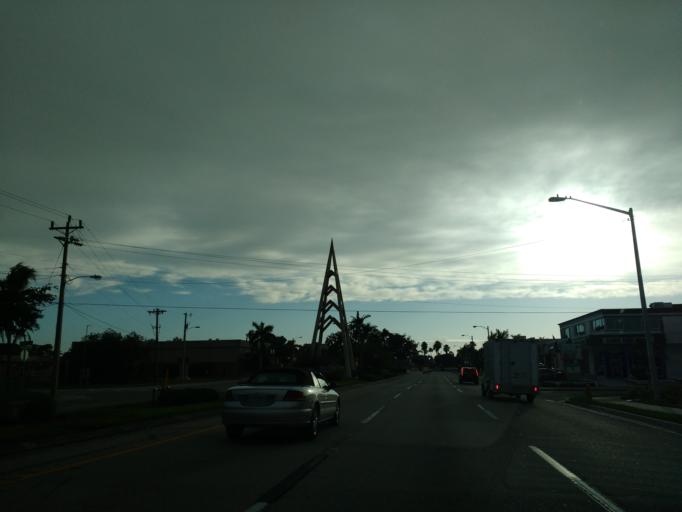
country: US
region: Florida
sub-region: Lee County
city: Cape Coral
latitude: 26.5628
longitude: -81.9413
